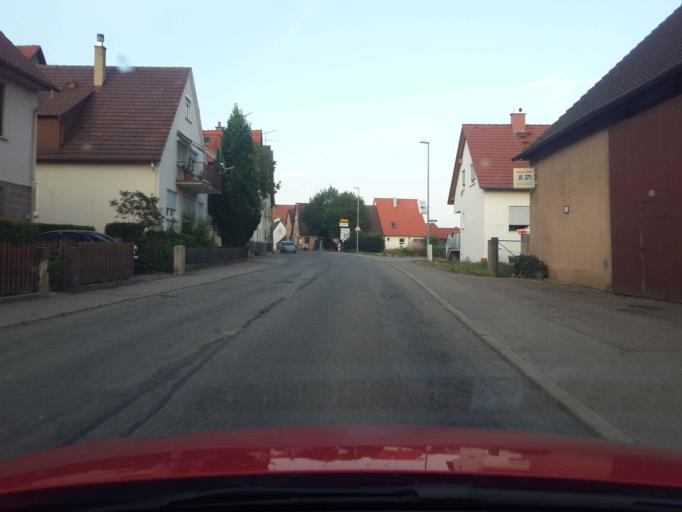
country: DE
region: Baden-Wuerttemberg
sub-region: Regierungsbezirk Stuttgart
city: Guglingen
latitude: 49.0684
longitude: 9.0248
